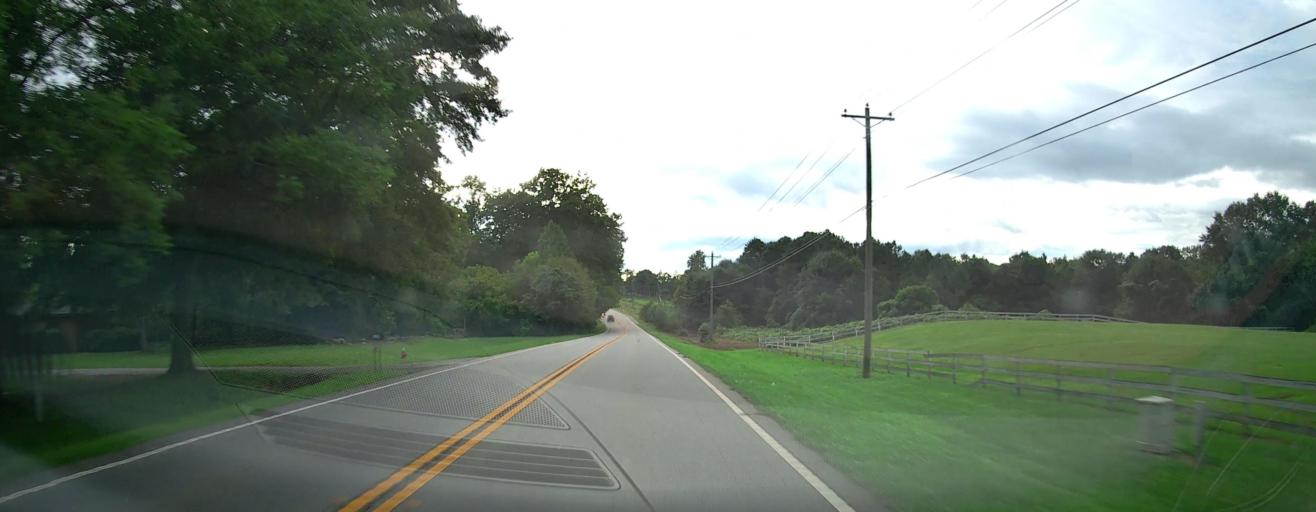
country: US
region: Georgia
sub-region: Houston County
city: Perry
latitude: 32.4539
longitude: -83.6849
